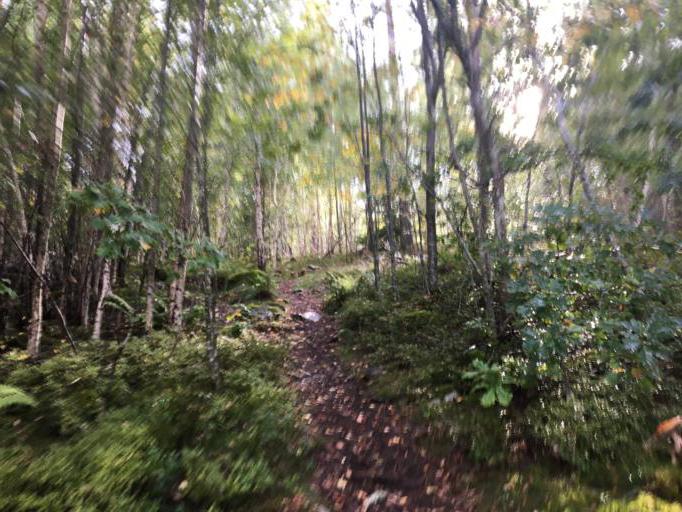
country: SE
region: Soedermanland
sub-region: Eskilstuna Kommun
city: Eskilstuna
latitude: 59.4589
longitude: 16.6547
